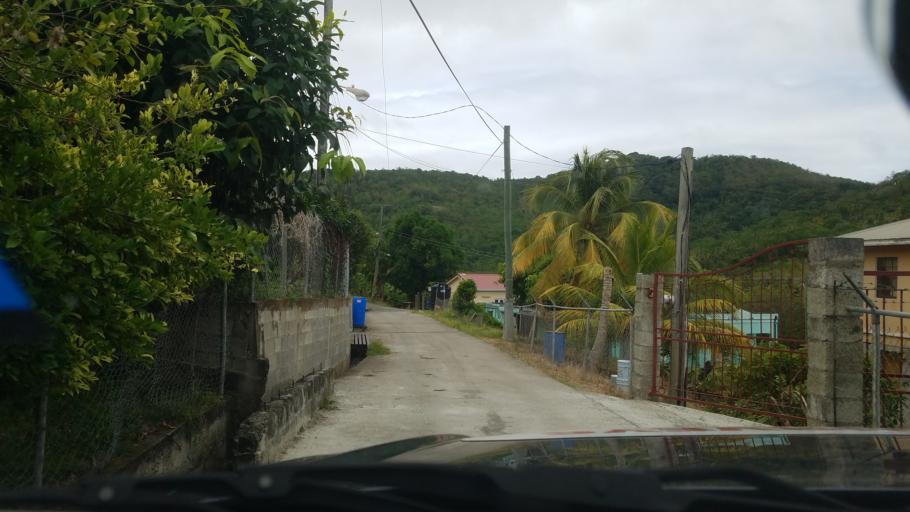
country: LC
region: Castries Quarter
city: Bisee
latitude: 14.0120
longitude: -60.9196
